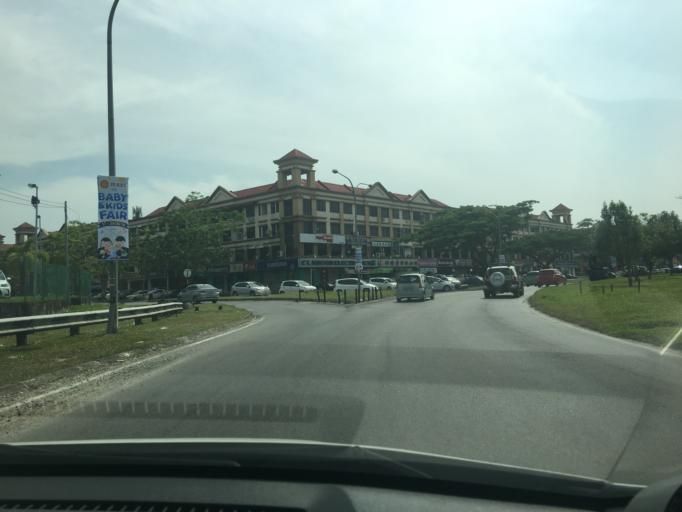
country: MY
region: Sarawak
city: Kuching
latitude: 1.5112
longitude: 110.3047
